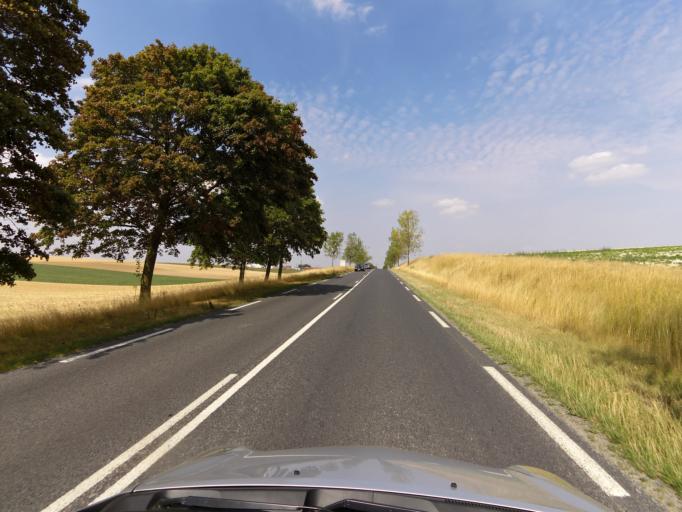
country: FR
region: Champagne-Ardenne
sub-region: Departement de la Marne
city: Rilly-la-Montagne
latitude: 49.1870
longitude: 4.0127
